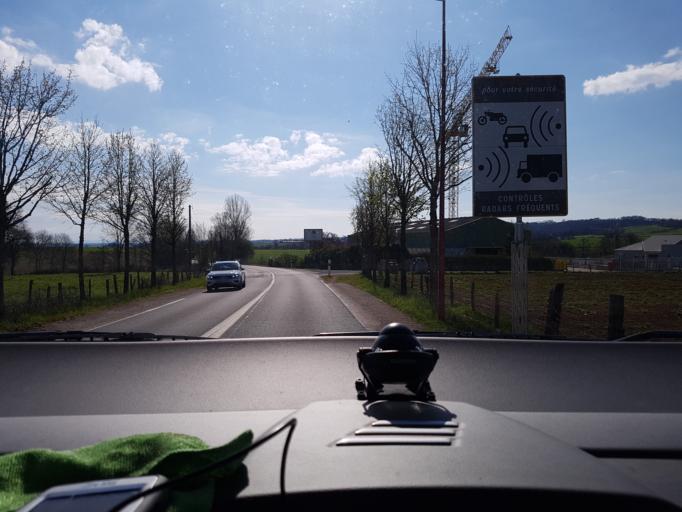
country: FR
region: Midi-Pyrenees
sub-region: Departement de l'Aveyron
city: Colombies
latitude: 44.3923
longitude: 2.3811
